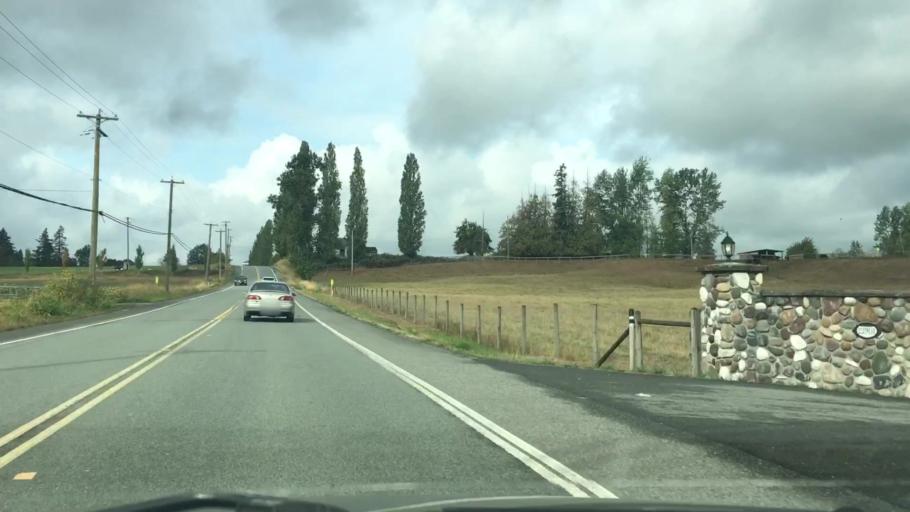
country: CA
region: British Columbia
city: Langley
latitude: 49.1043
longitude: -122.5901
